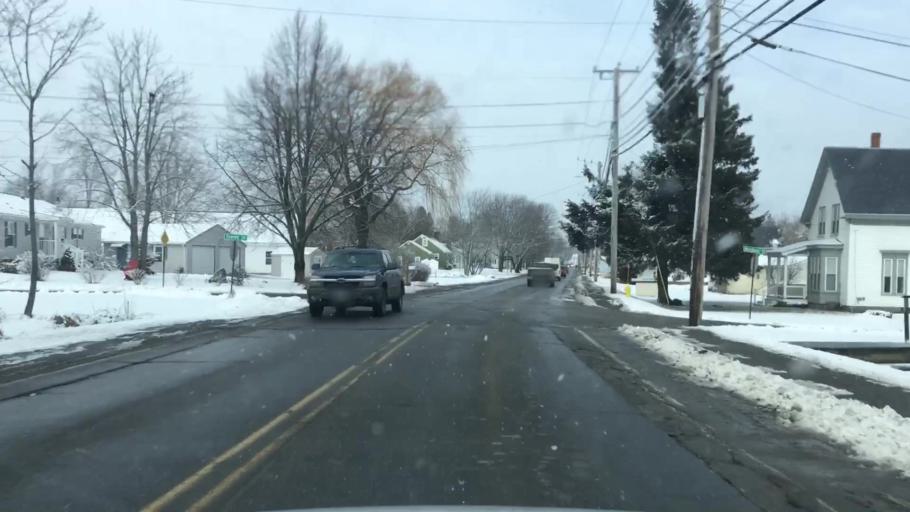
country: US
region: Maine
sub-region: Knox County
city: Rockland
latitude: 44.0926
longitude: -69.1106
